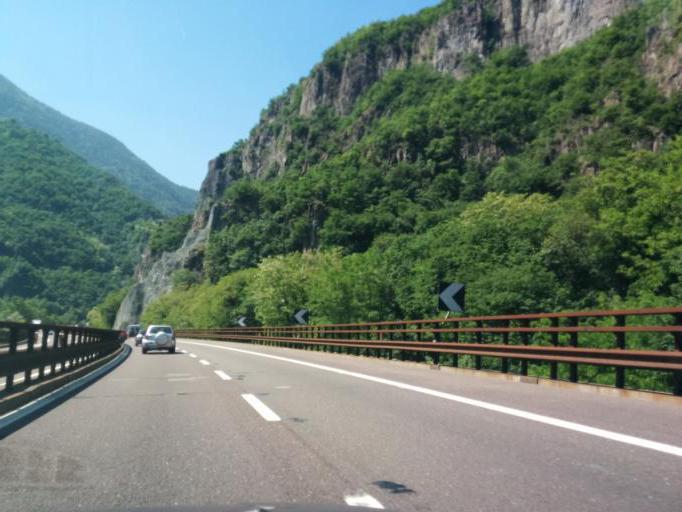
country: IT
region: Trentino-Alto Adige
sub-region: Bolzano
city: Cornedo All'Isarco
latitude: 46.4959
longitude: 11.4420
